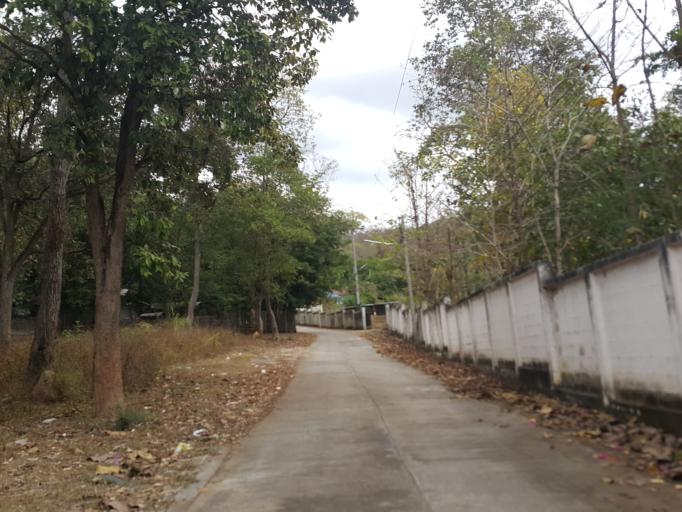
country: TH
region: Chiang Mai
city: San Sai
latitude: 18.8695
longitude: 99.1390
